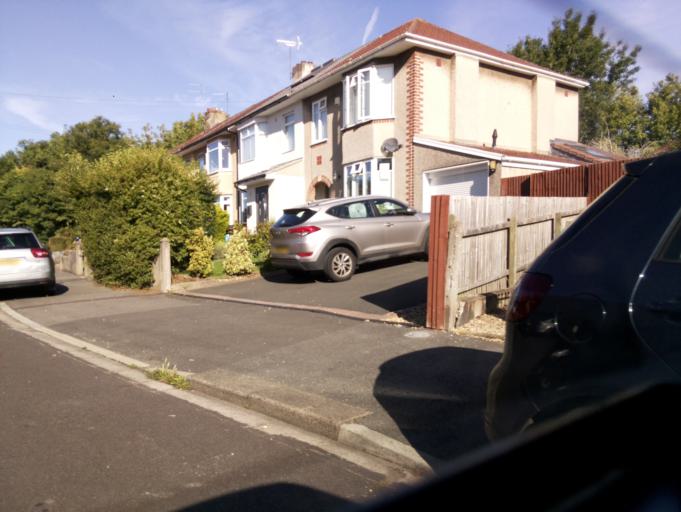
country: GB
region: England
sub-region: Bath and North East Somerset
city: Whitchurch
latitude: 51.4318
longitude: -2.5523
